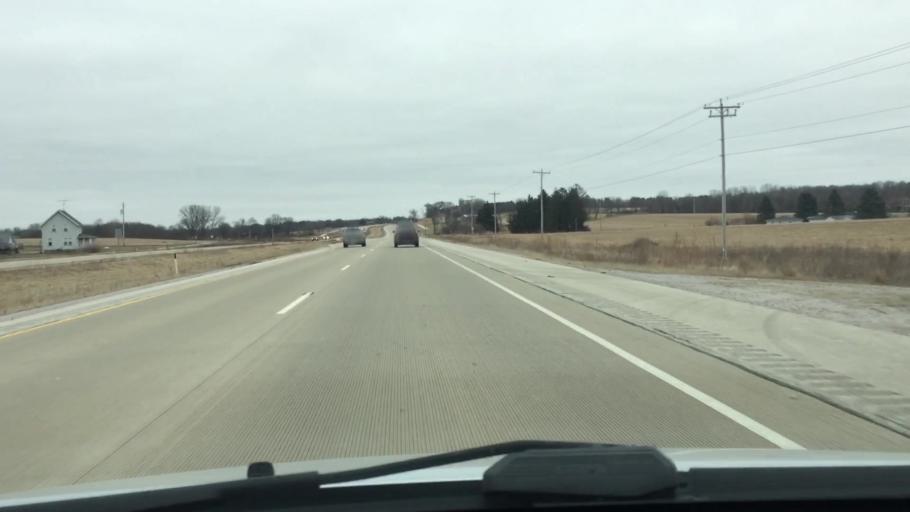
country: US
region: Wisconsin
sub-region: Jefferson County
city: Johnson Creek
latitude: 43.1070
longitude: -88.7548
